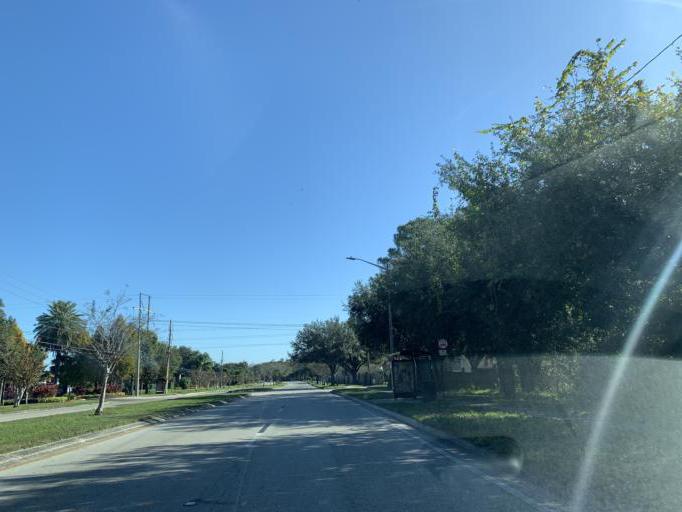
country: US
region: Florida
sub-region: Orange County
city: Oak Ridge
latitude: 28.4939
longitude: -81.4562
